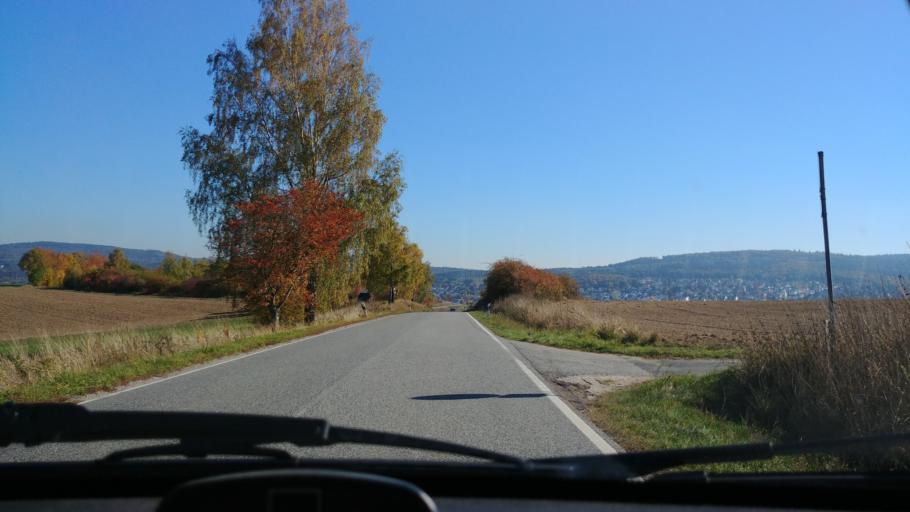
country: DE
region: Hesse
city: Taunusstein
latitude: 50.1473
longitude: 8.1257
